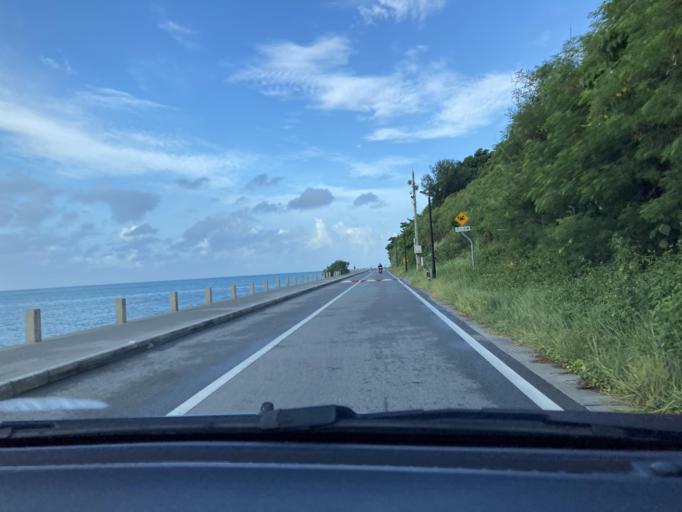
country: JP
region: Okinawa
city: Tomigusuku
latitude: 26.1740
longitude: 127.6446
